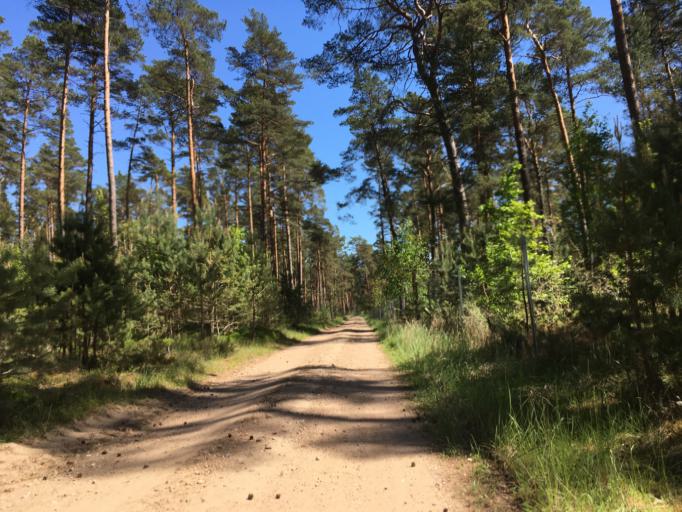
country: DE
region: Brandenburg
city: Friedrichswalde
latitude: 52.9852
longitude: 13.6134
